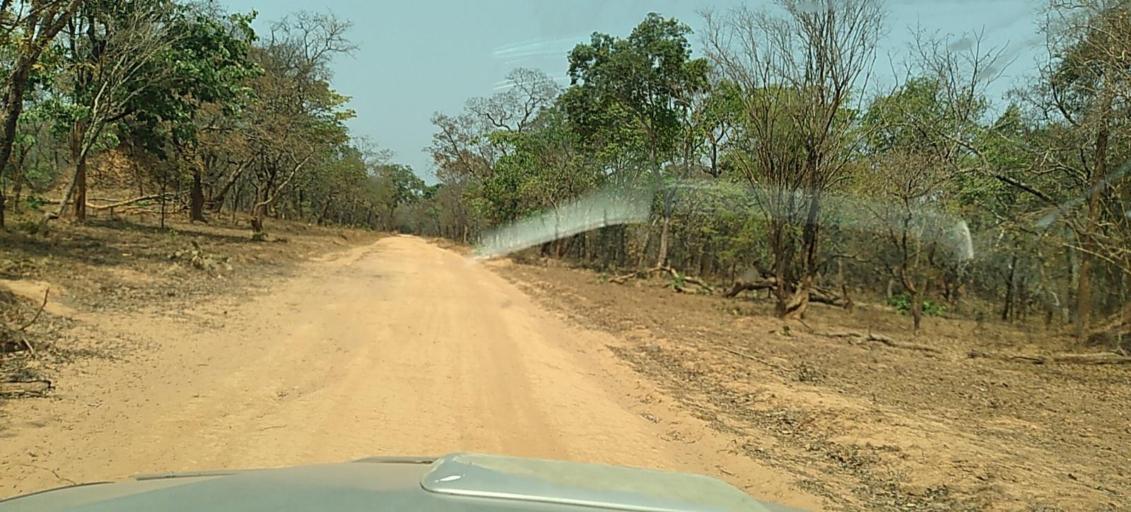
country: ZM
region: North-Western
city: Kasempa
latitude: -13.6640
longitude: 26.2789
